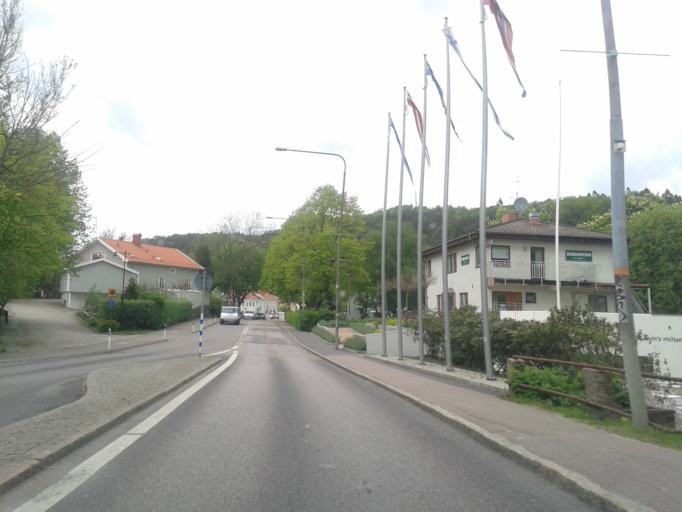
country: SE
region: Vaestra Goetaland
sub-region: Kungalvs Kommun
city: Kungalv
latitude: 57.8630
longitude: 11.9964
